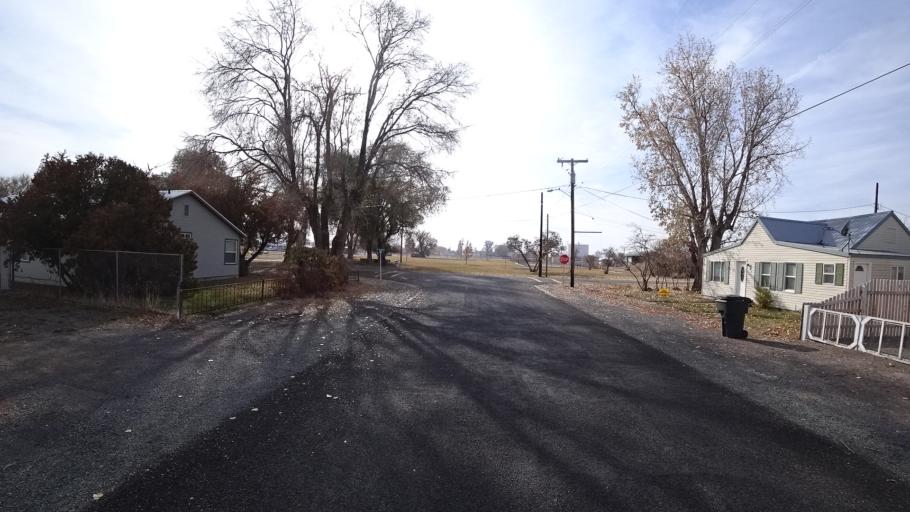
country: US
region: California
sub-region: Siskiyou County
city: Tulelake
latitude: 41.9576
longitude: -121.4803
